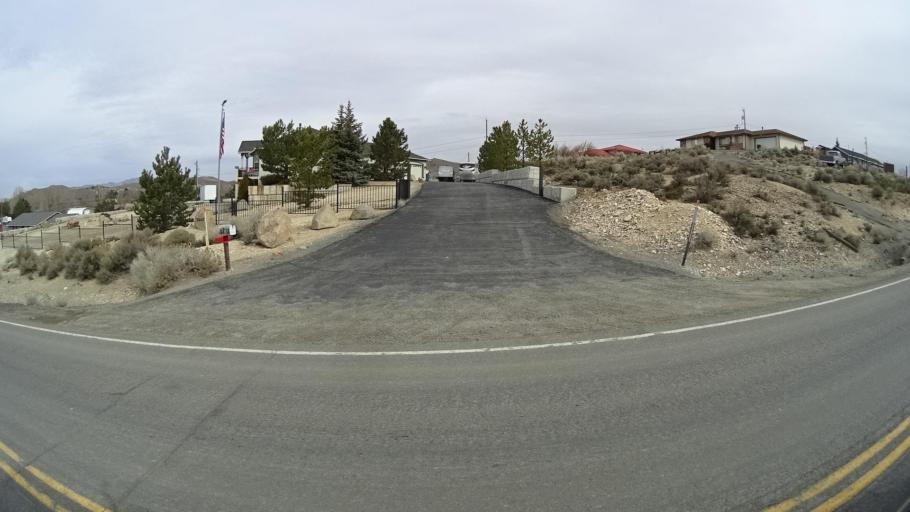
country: US
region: Nevada
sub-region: Washoe County
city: Golden Valley
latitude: 39.6078
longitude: -119.8151
